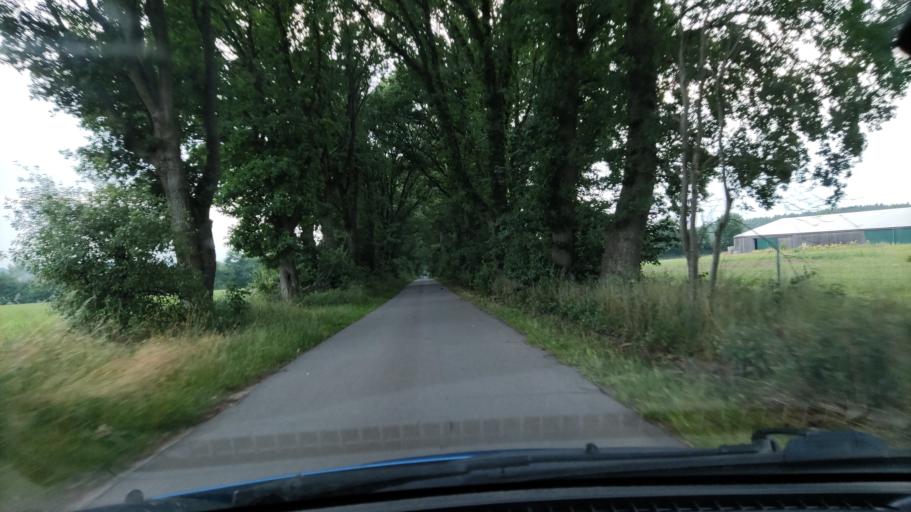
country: DE
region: Lower Saxony
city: Amelinghausen
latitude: 53.1321
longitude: 10.2467
